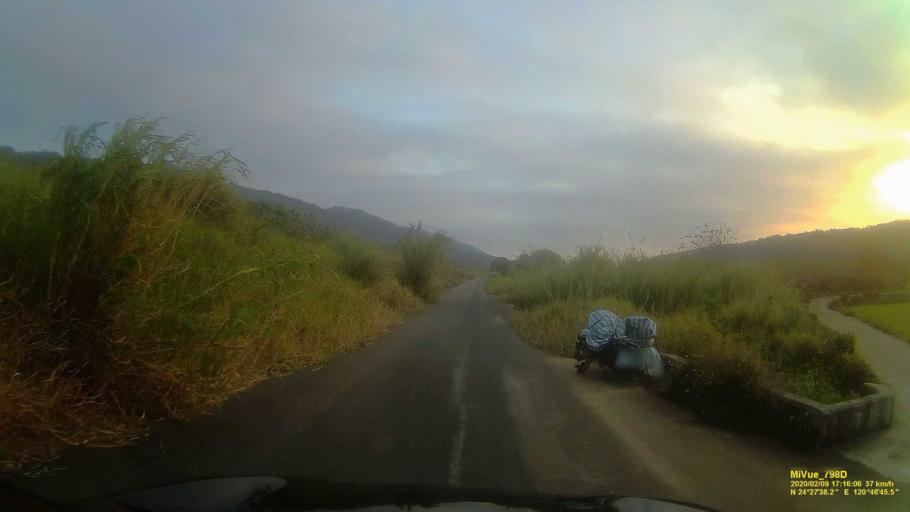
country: TW
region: Taiwan
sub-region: Miaoli
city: Miaoli
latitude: 24.4604
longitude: 120.7793
